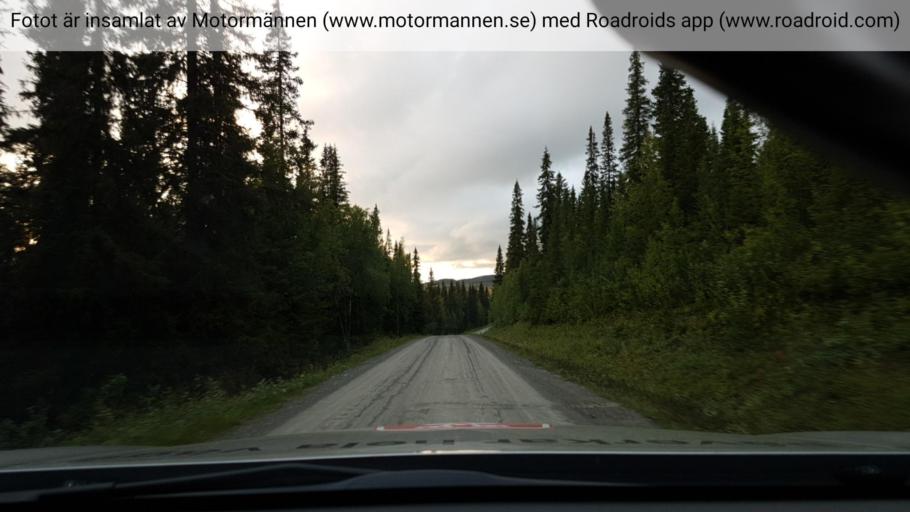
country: SE
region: Vaesterbotten
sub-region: Vilhelmina Kommun
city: Sjoberg
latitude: 65.5432
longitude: 15.4233
